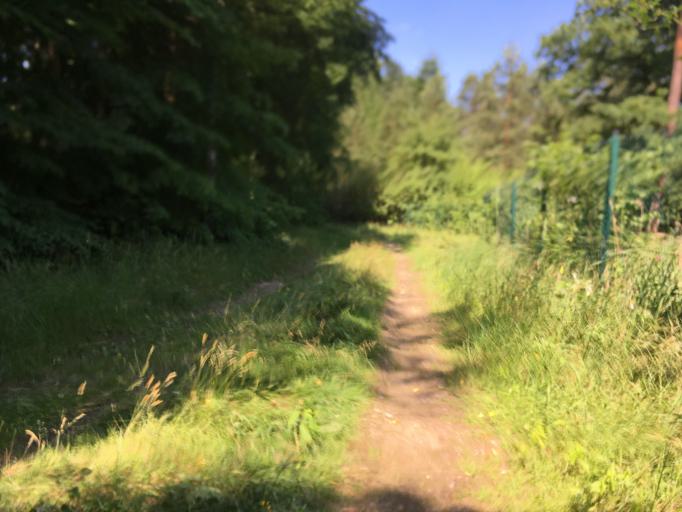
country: DE
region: Brandenburg
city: Marienwerder
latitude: 52.9208
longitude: 13.6604
